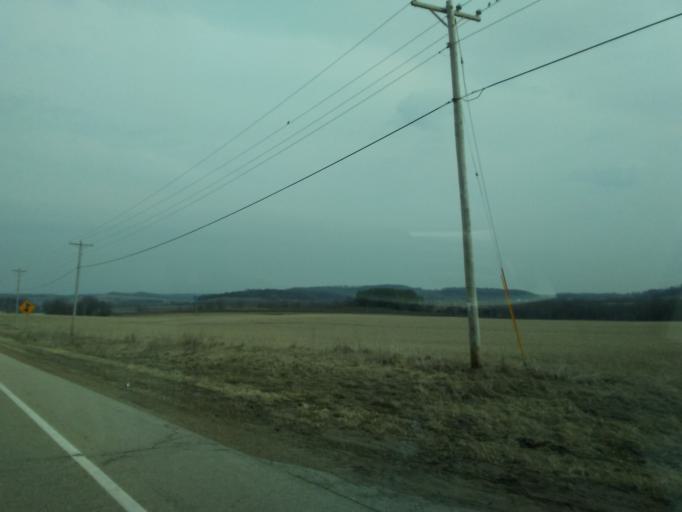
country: US
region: Wisconsin
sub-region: Columbia County
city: Lodi
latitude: 43.2688
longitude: -89.5212
